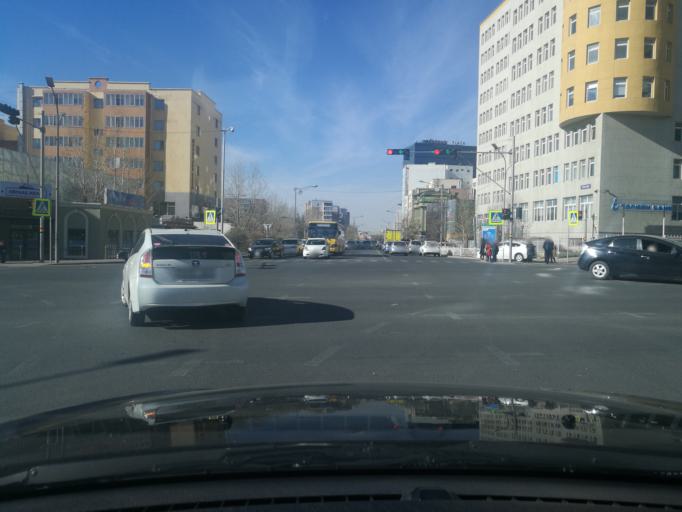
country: MN
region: Ulaanbaatar
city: Ulaanbaatar
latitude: 47.9133
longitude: 106.8950
